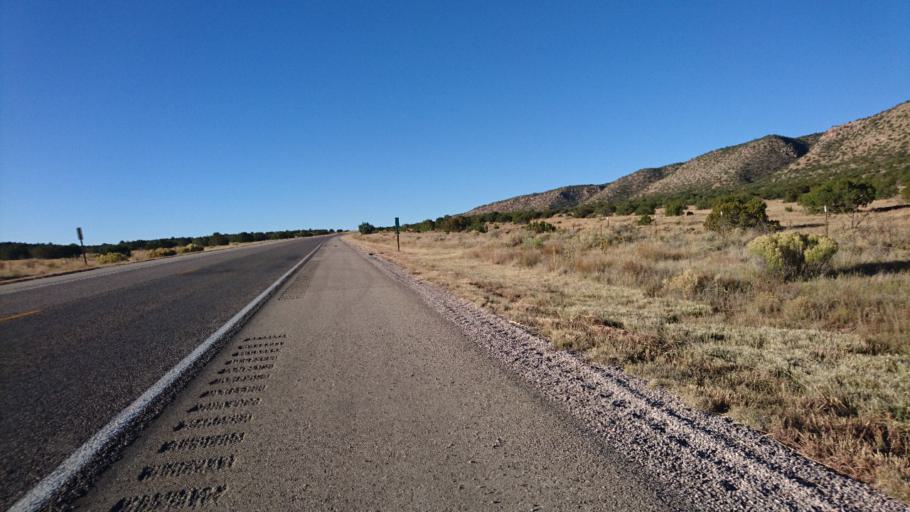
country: US
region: New Mexico
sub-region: Cibola County
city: Grants
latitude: 35.0080
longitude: -107.8912
